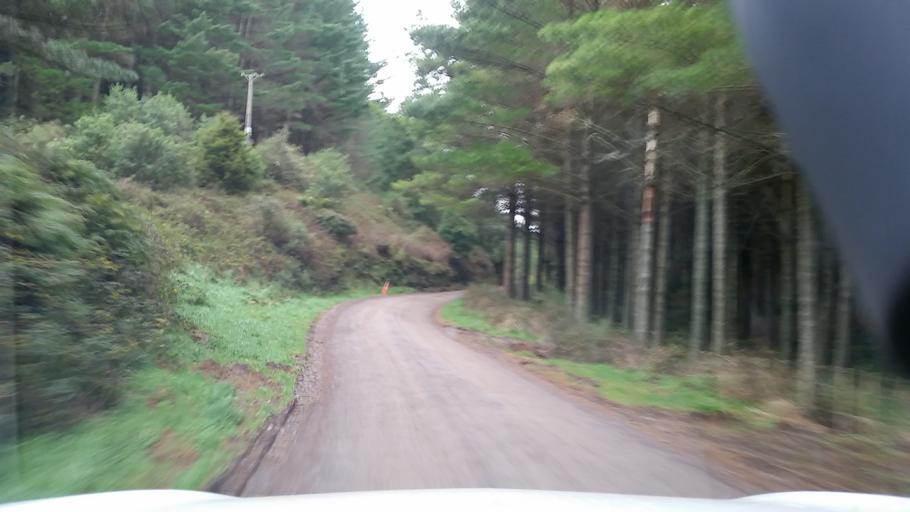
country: NZ
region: Bay of Plenty
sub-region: Rotorua District
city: Rotorua
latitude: -38.2201
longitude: 176.1593
